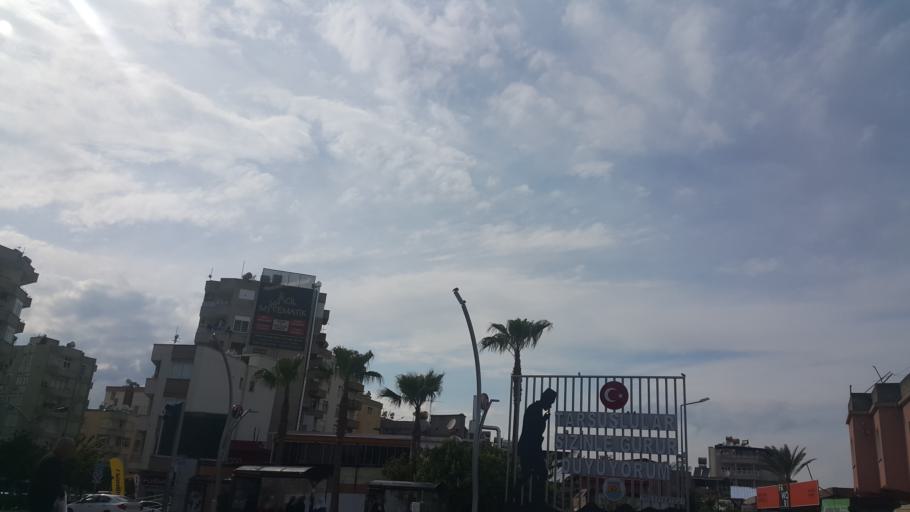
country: TR
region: Mersin
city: Tarsus
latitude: 36.9180
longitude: 34.8914
